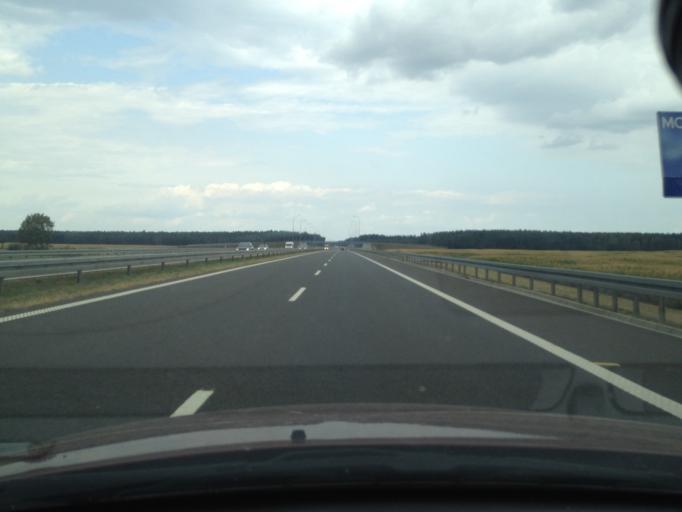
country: PL
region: West Pomeranian Voivodeship
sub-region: Powiat pyrzycki
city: Bielice
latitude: 53.1435
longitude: 14.7181
